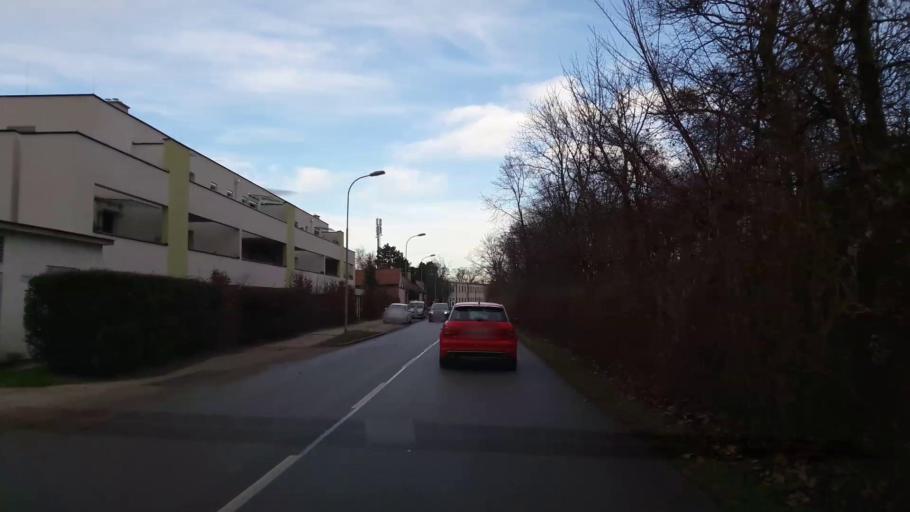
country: AT
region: Lower Austria
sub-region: Politischer Bezirk Baden
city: Ebreichsdorf
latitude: 47.9583
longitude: 16.4268
